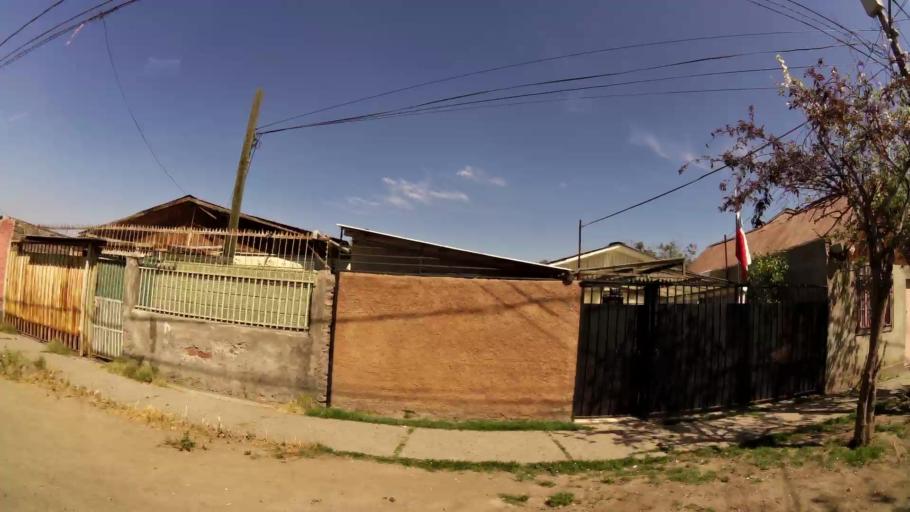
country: CL
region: Santiago Metropolitan
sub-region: Provincia de Santiago
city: Santiago
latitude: -33.5112
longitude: -70.6425
